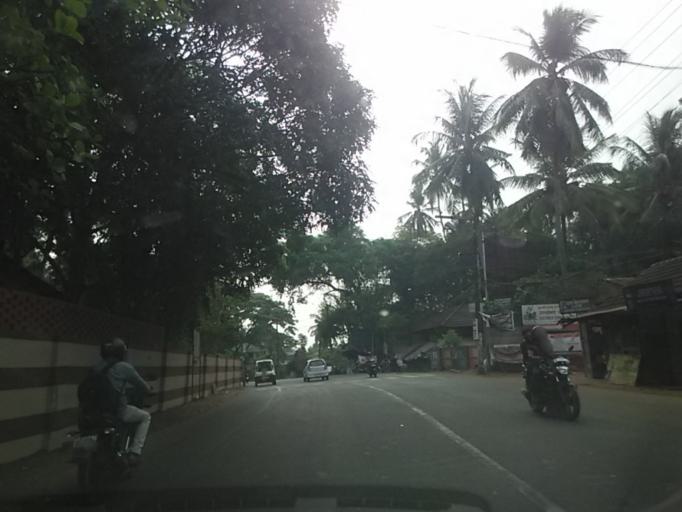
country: IN
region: Kerala
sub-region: Kozhikode
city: Kozhikode
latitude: 11.2870
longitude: 75.8038
